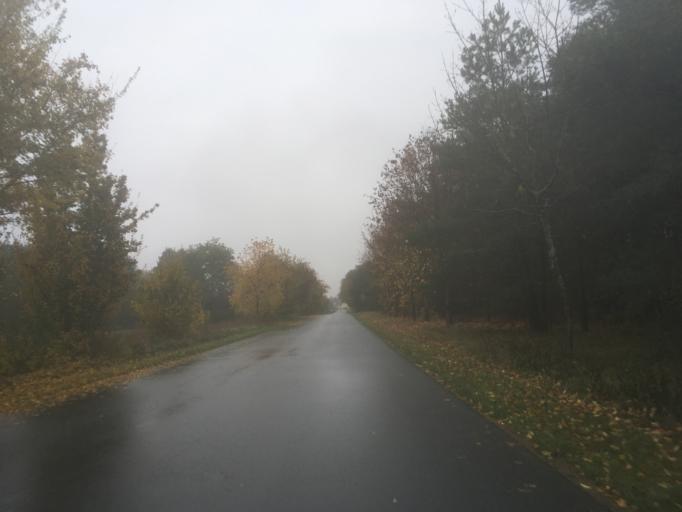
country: DE
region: Brandenburg
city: Schlepzig
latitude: 52.0202
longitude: 13.9760
